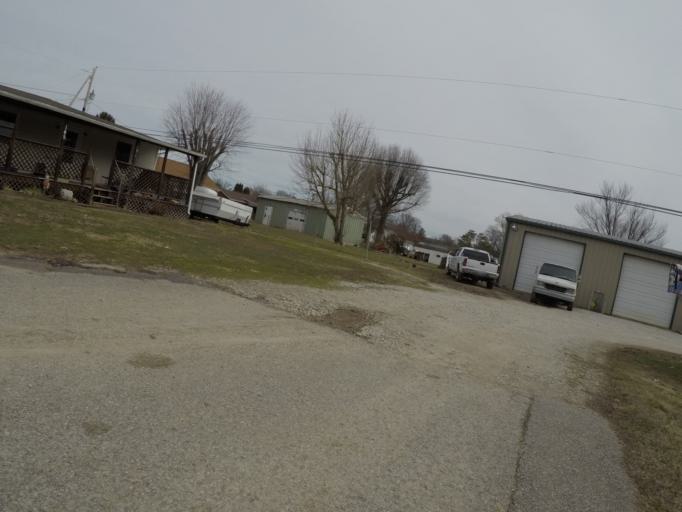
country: US
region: West Virginia
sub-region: Cabell County
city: Pea Ridge
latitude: 38.4529
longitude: -82.3373
